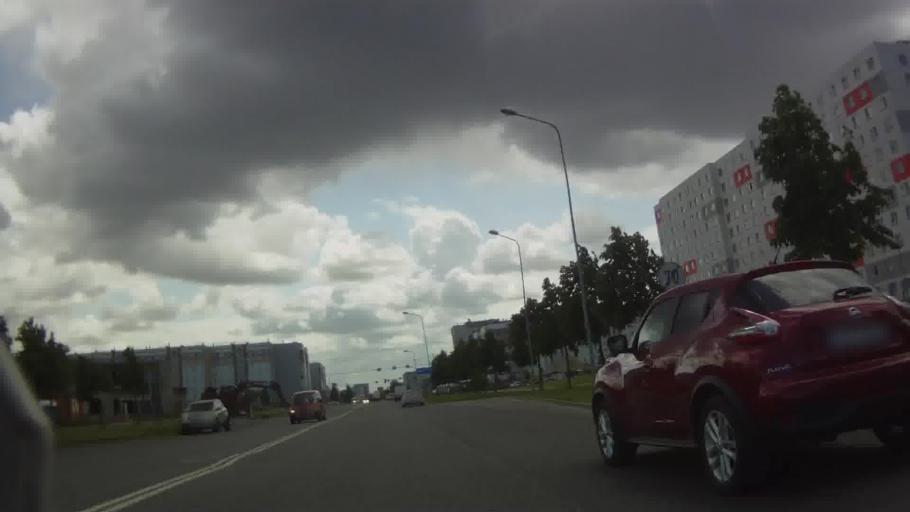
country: LV
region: Stopini
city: Ulbroka
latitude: 56.9472
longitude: 24.2183
